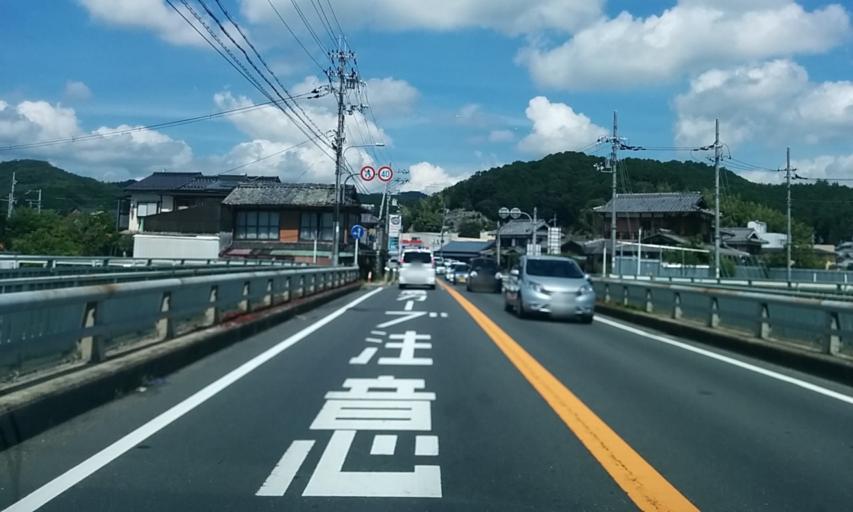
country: JP
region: Kyoto
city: Kameoka
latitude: 35.1108
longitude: 135.4702
